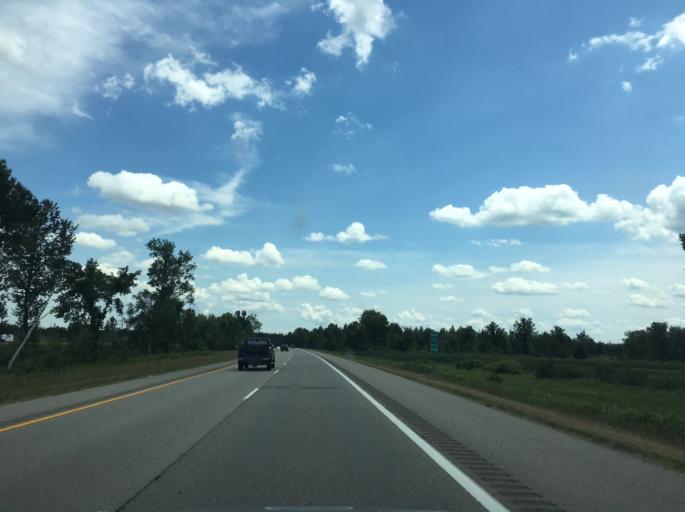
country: US
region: Michigan
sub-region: Ogemaw County
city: Skidway Lake
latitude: 44.0881
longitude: -84.1061
